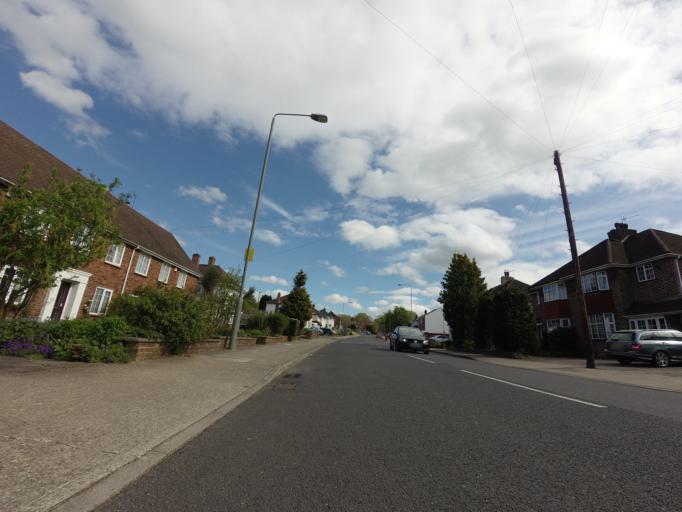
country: GB
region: England
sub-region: Greater London
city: Orpington
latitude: 51.3714
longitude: 0.1132
